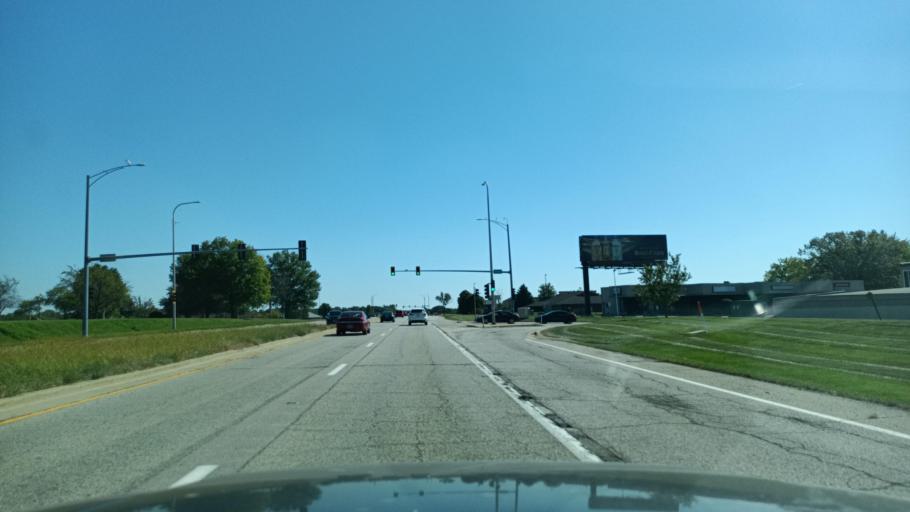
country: US
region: Illinois
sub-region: Peoria County
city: West Peoria
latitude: 40.7725
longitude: -89.6614
